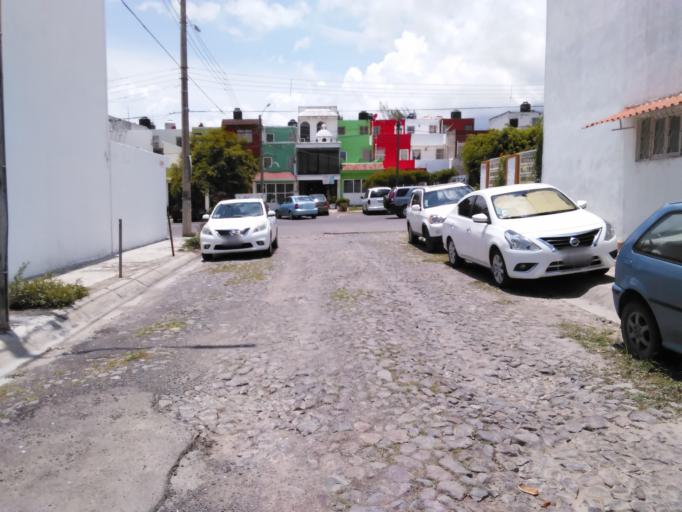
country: MX
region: Nayarit
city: Tepic
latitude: 21.5164
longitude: -104.9169
